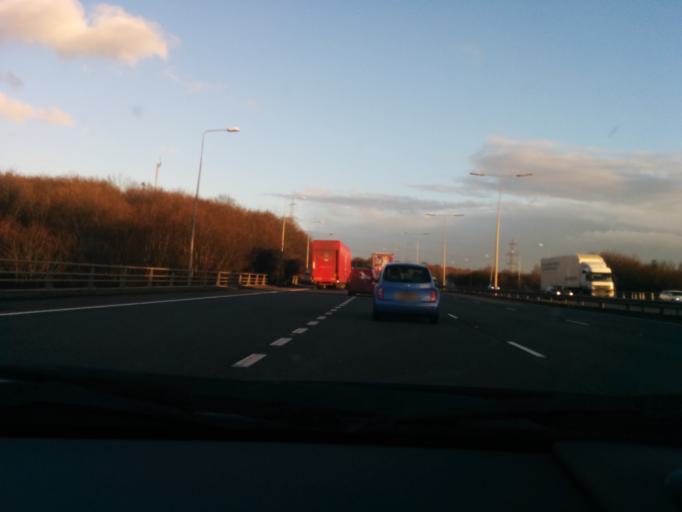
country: GB
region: England
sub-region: Buckinghamshire
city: Denham
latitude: 51.5609
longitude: -0.5315
